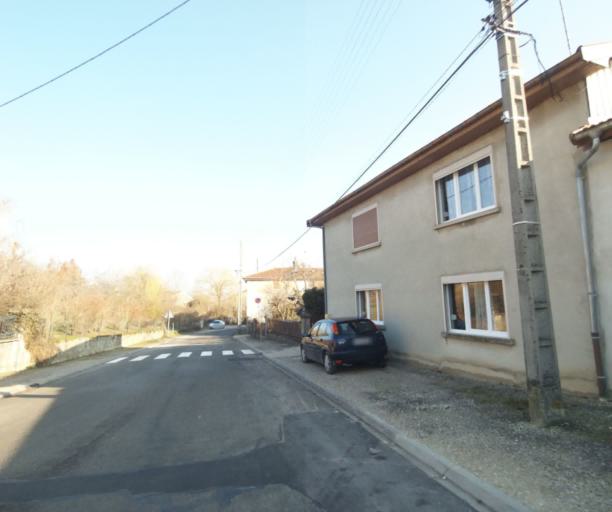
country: FR
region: Champagne-Ardenne
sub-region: Departement de la Haute-Marne
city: Wassy
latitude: 48.5139
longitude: 4.9172
